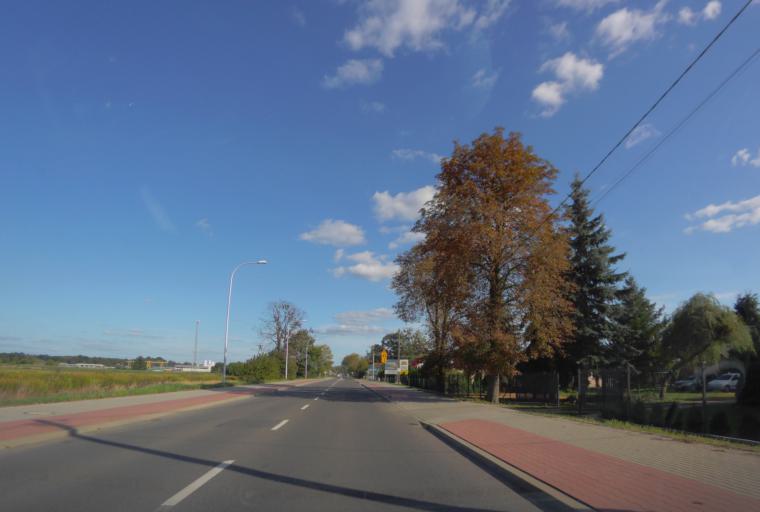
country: PL
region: Subcarpathian Voivodeship
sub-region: Tarnobrzeg
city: Tarnobrzeg
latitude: 50.5637
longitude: 21.7340
